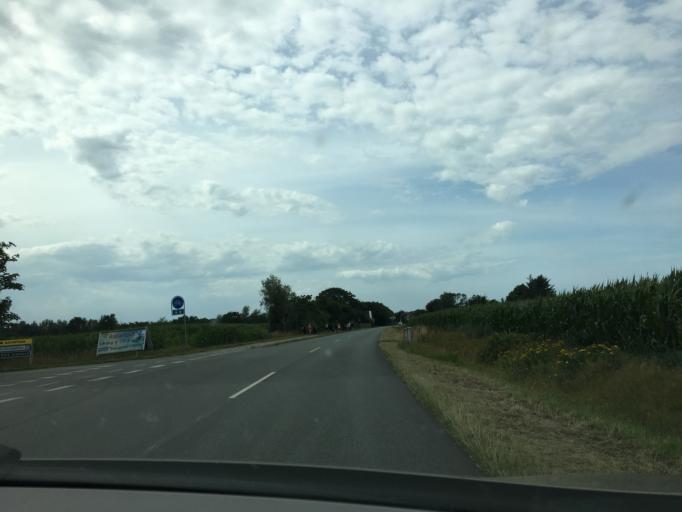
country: DK
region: South Denmark
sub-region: Varde Kommune
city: Oksbol
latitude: 55.8459
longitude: 8.2914
